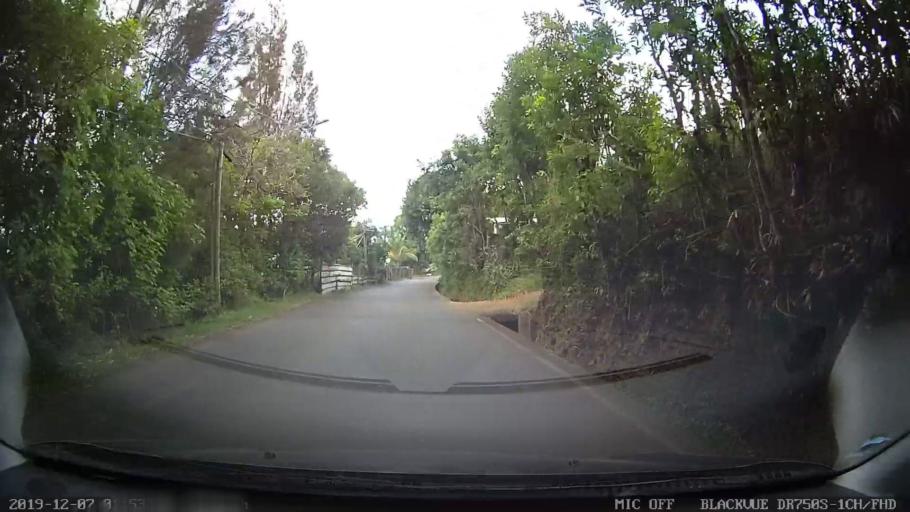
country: RE
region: Reunion
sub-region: Reunion
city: Sainte-Marie
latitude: -20.9367
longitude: 55.5340
